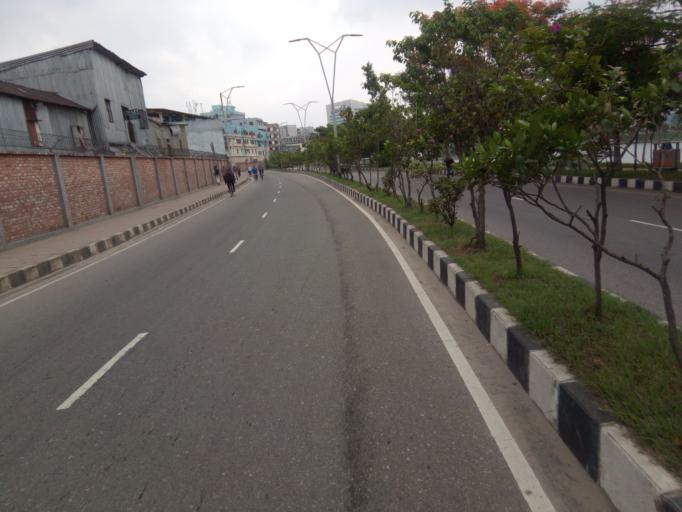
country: BD
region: Dhaka
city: Paltan
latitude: 23.7663
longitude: 90.4105
